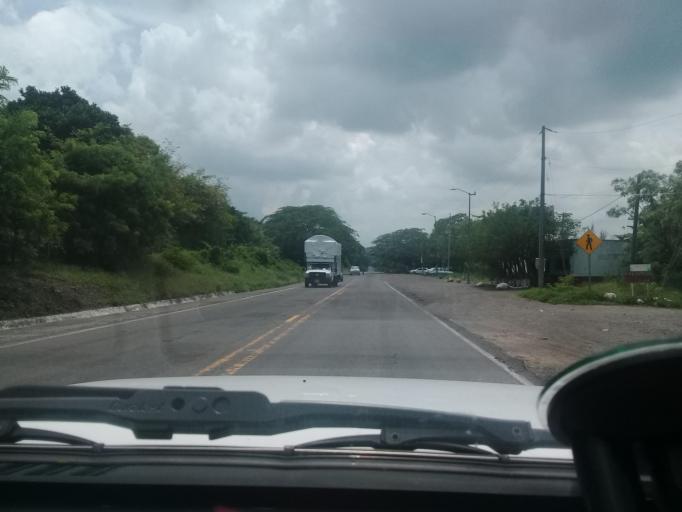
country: MX
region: Veracruz
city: Paso de Ovejas
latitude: 19.2906
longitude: -96.4470
